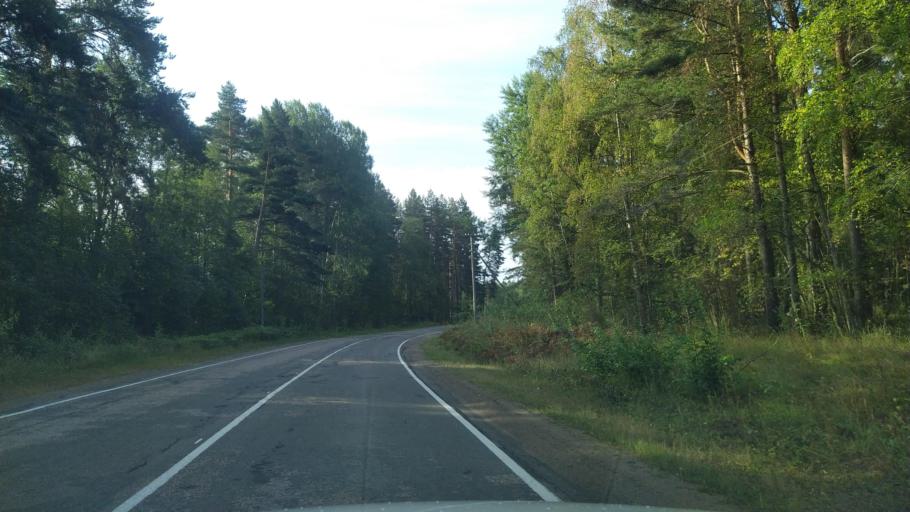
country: RU
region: Leningrad
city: Priozersk
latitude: 60.9931
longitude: 30.2563
